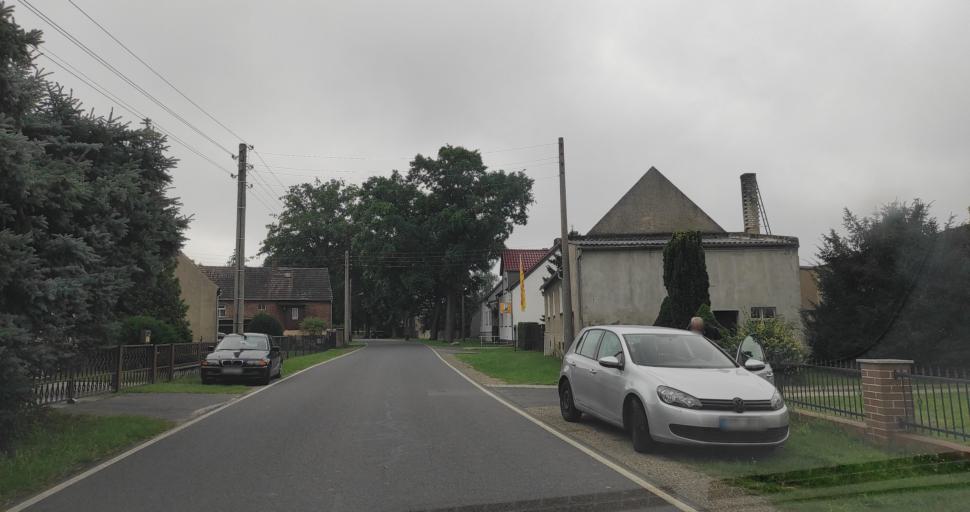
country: DE
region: Brandenburg
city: Forst
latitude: 51.6896
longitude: 14.6325
